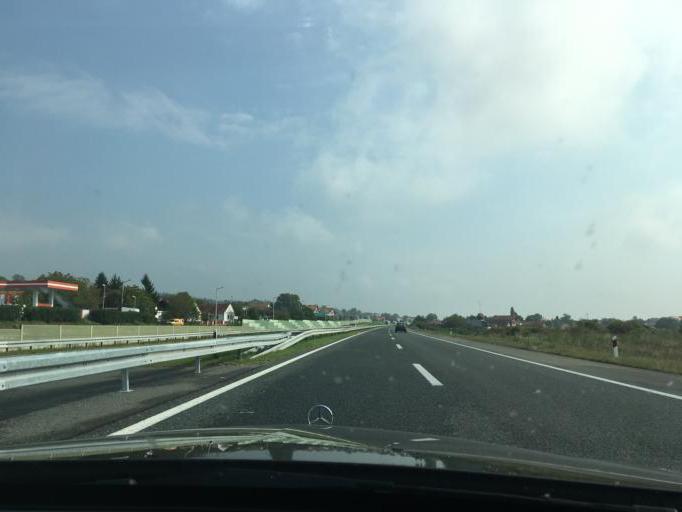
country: HR
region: Brodsko-Posavska
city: Slobodnica
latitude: 45.1779
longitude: 17.9663
